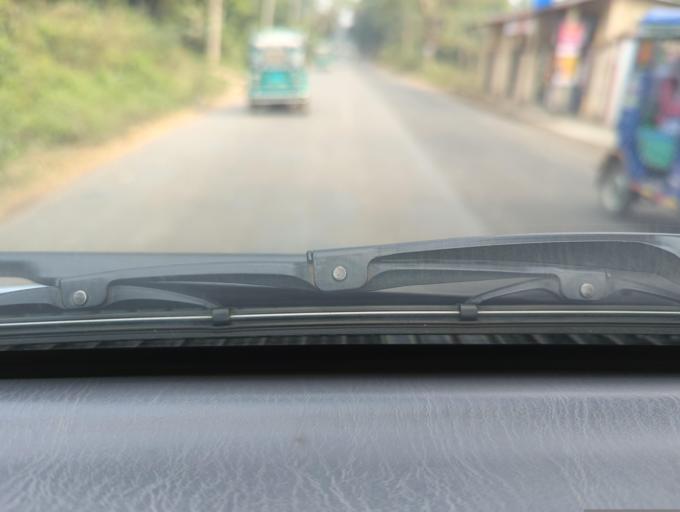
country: BD
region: Sylhet
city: Maulavi Bazar
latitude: 24.4976
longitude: 91.7385
